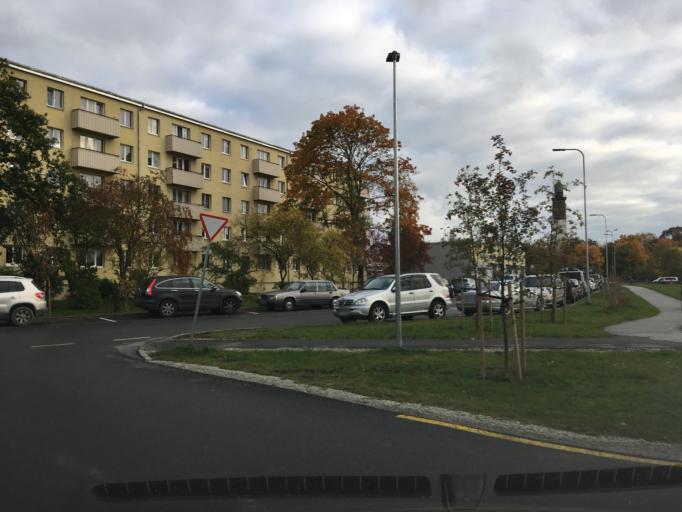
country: EE
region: Harju
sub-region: Tallinna linn
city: Tallinn
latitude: 59.4301
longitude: 24.8046
